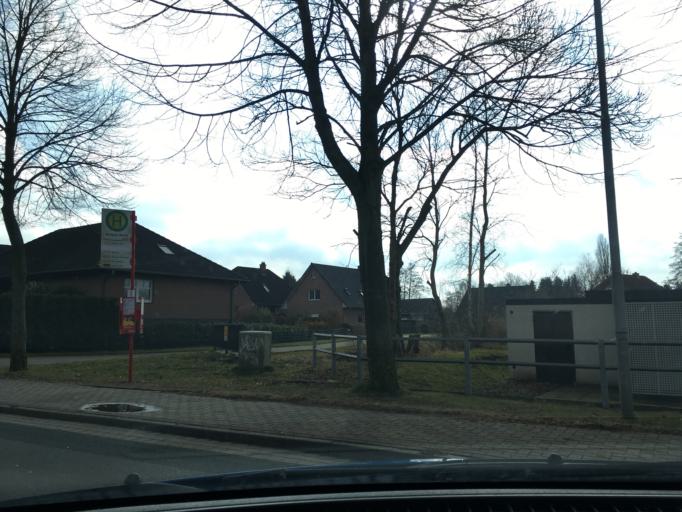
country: DE
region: Lower Saxony
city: Winsen
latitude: 53.3520
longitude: 10.2314
